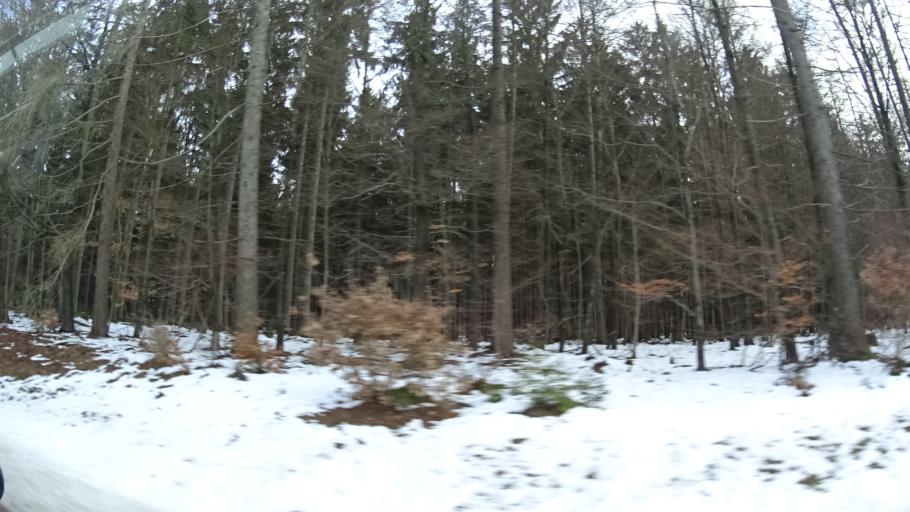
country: DE
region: Baden-Wuerttemberg
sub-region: Karlsruhe Region
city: Fahrenbach
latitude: 49.4859
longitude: 9.1481
